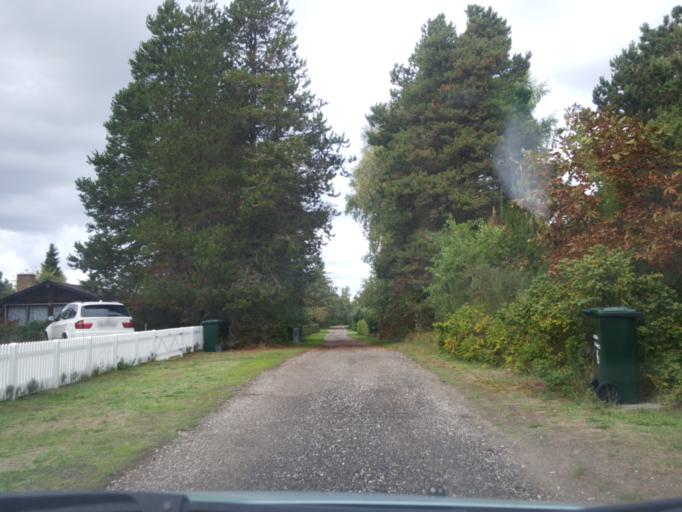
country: DK
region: Zealand
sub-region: Guldborgsund Kommune
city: Nykobing Falster
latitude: 54.6546
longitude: 11.9490
